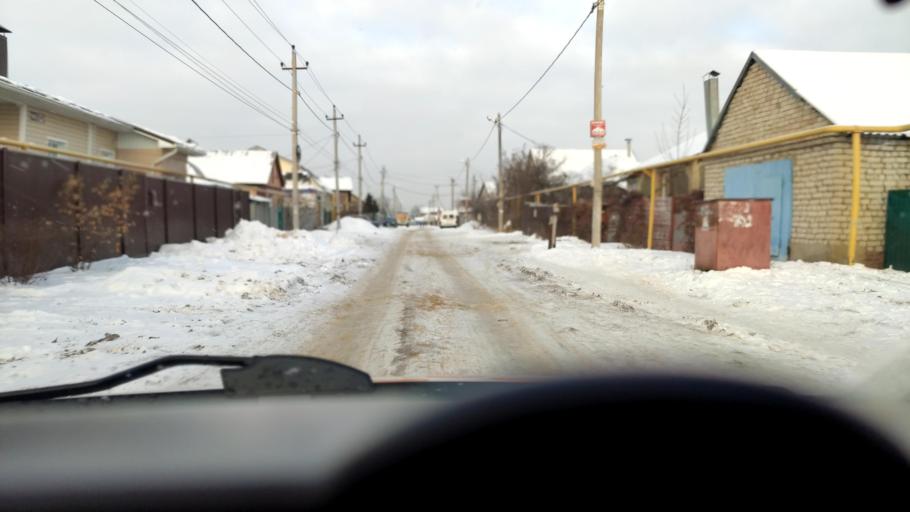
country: RU
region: Voronezj
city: Podgornoye
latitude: 51.7272
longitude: 39.1546
